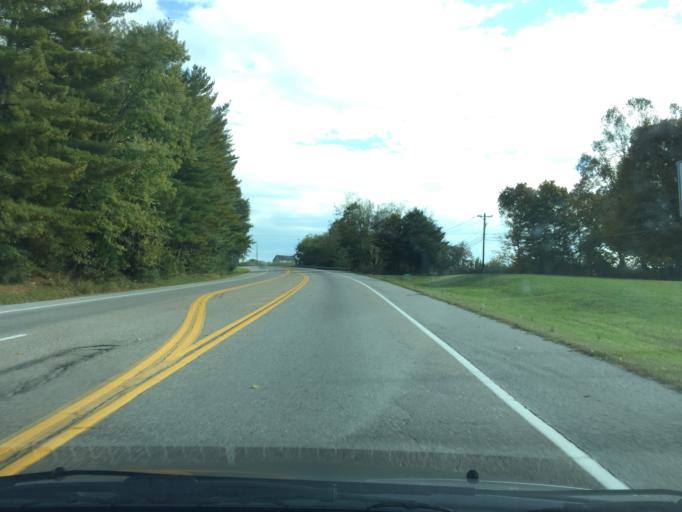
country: US
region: Tennessee
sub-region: Loudon County
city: Loudon
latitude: 35.7243
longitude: -84.3776
